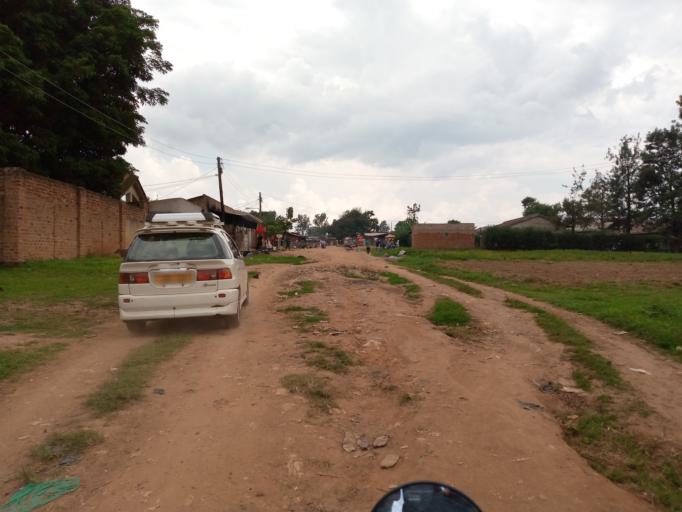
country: UG
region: Eastern Region
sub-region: Mbale District
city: Mbale
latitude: 1.0857
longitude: 34.1693
